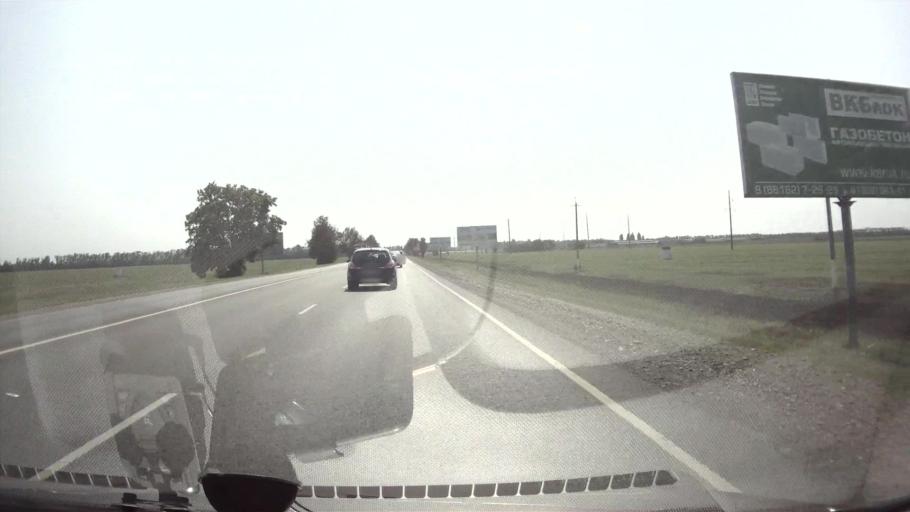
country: RU
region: Krasnodarskiy
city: Vasyurinskaya
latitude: 45.1087
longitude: 39.3882
